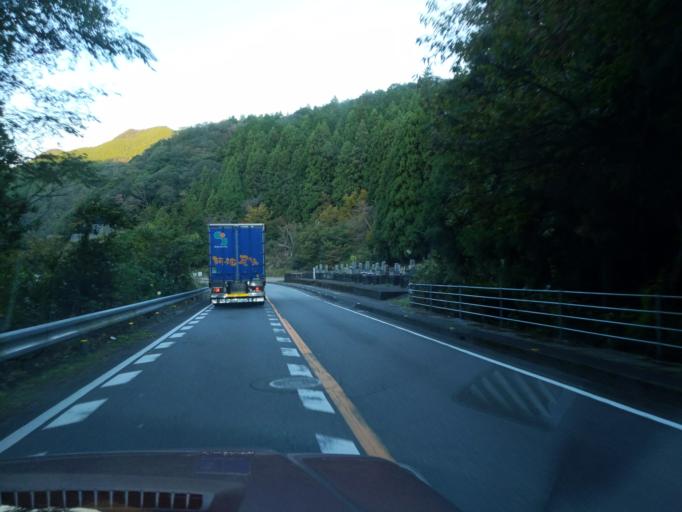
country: JP
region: Tokushima
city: Anan
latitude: 33.7178
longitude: 134.4913
